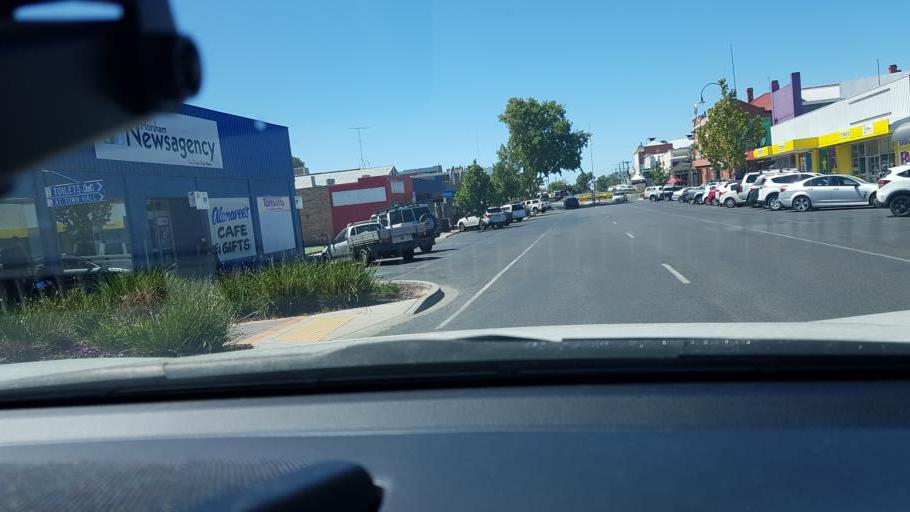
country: AU
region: Victoria
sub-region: Horsham
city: Horsham
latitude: -36.7154
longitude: 142.1982
